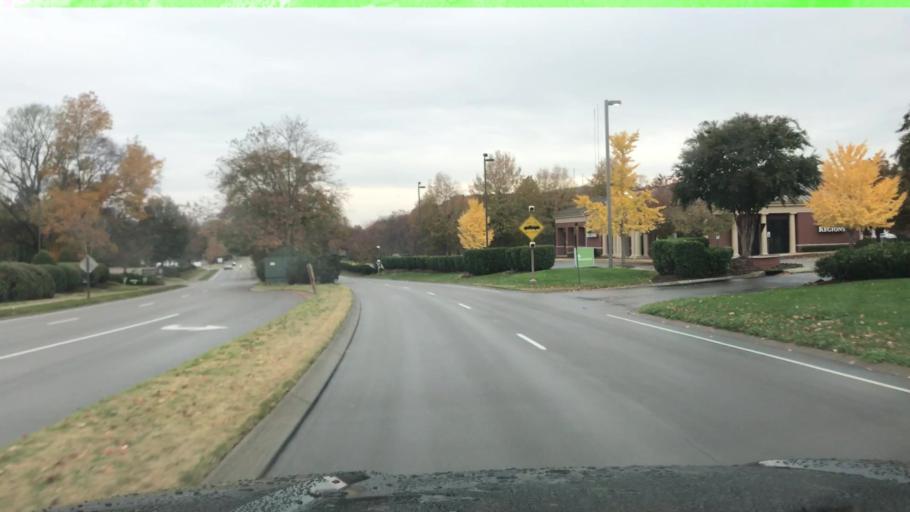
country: US
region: Tennessee
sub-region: Williamson County
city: Brentwood
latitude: 36.0348
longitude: -86.8032
